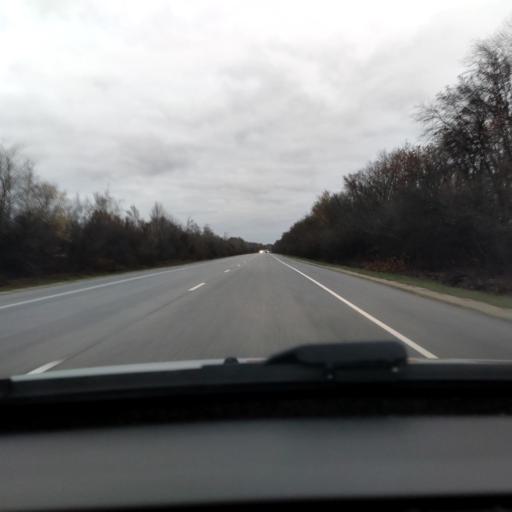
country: RU
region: Lipetsk
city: Borinskoye
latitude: 52.3618
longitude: 39.2016
